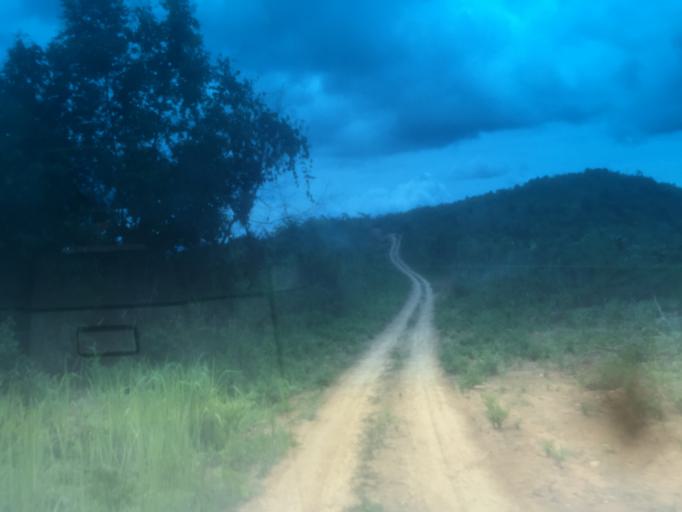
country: LA
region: Phongsali
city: Khoa
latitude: 20.9270
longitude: 102.5401
